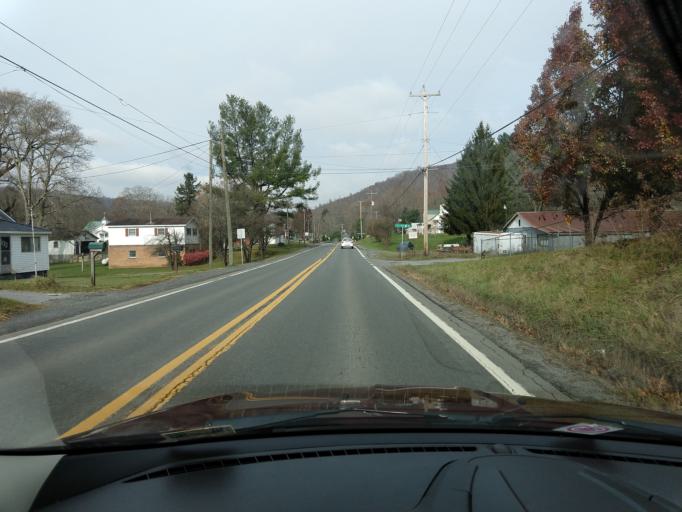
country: US
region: West Virginia
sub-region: Greenbrier County
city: Rainelle
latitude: 37.9819
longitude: -80.7161
